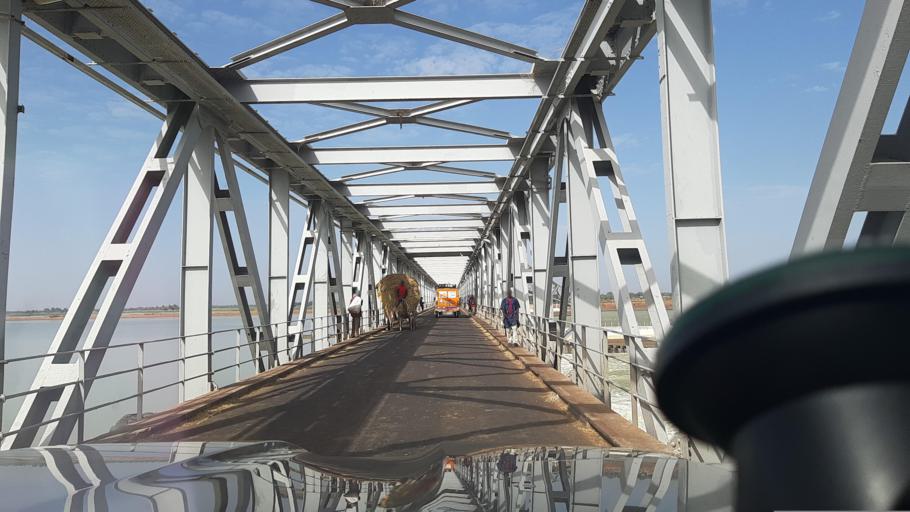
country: ML
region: Segou
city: Markala
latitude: 13.6803
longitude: -6.0817
